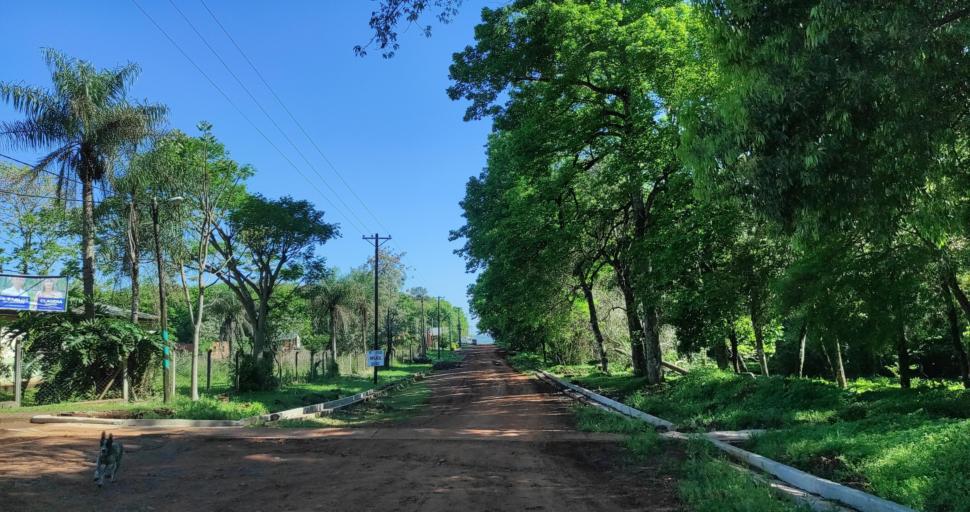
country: AR
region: Misiones
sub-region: Departamento de Candelaria
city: Loreto
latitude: -27.3314
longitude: -55.5228
